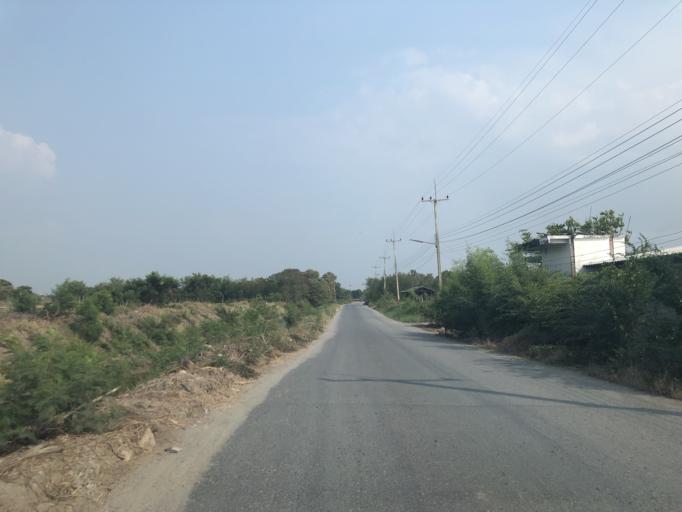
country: TH
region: Chachoengsao
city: Bang Pakong
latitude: 13.5100
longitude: 100.9332
